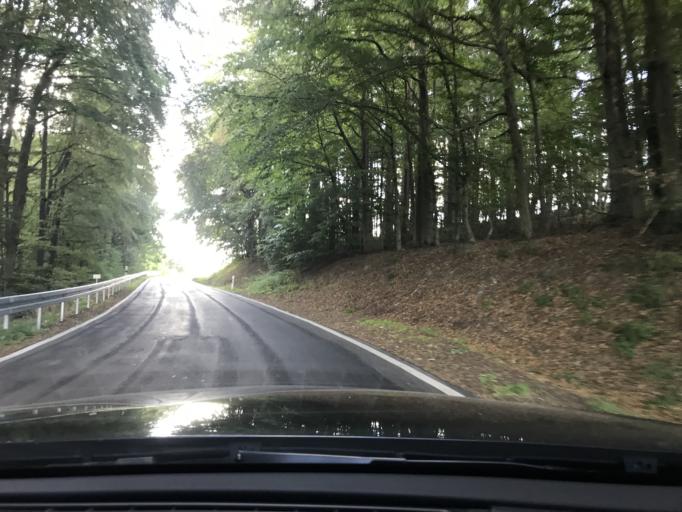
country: DE
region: Bavaria
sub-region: Regierungsbezirk Unterfranken
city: Kirchlauter
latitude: 50.0722
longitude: 10.6644
